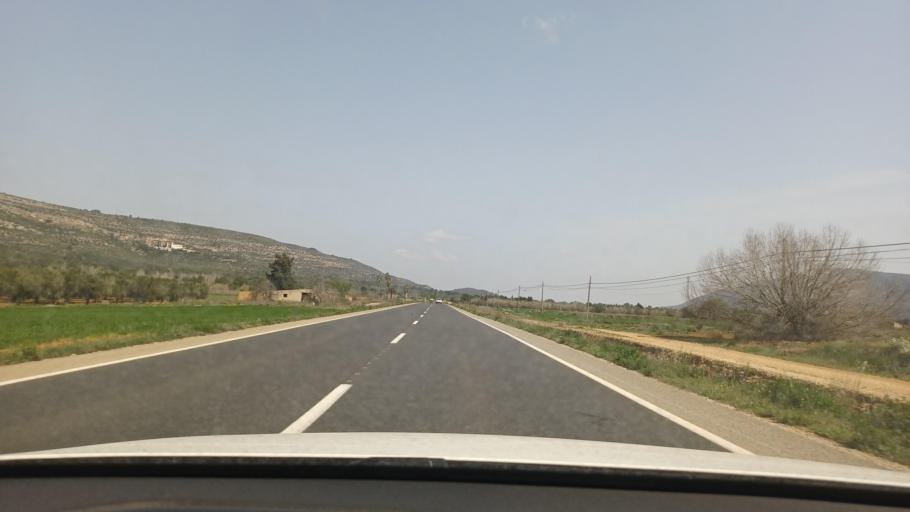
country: ES
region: Catalonia
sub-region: Provincia de Tarragona
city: Ulldecona
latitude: 40.6142
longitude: 0.4657
